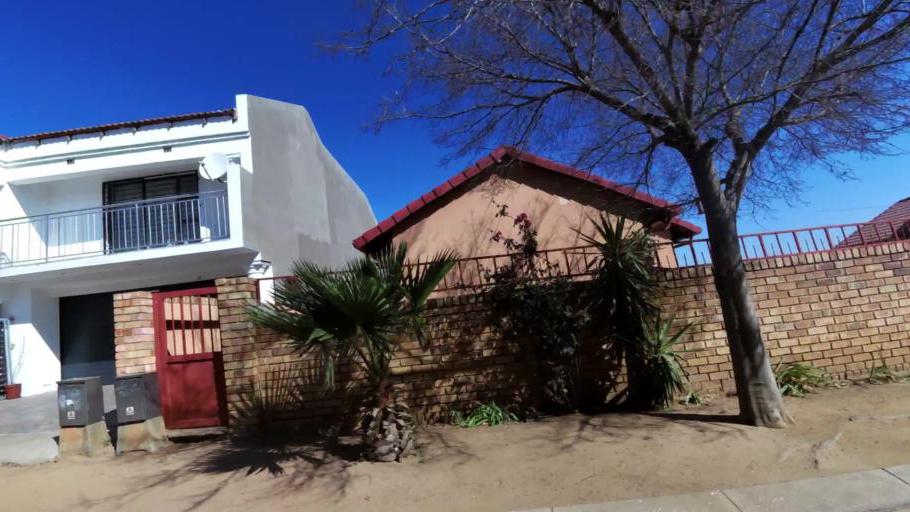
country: ZA
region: Gauteng
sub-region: City of Johannesburg Metropolitan Municipality
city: Johannesburg
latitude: -26.2497
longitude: 27.9780
